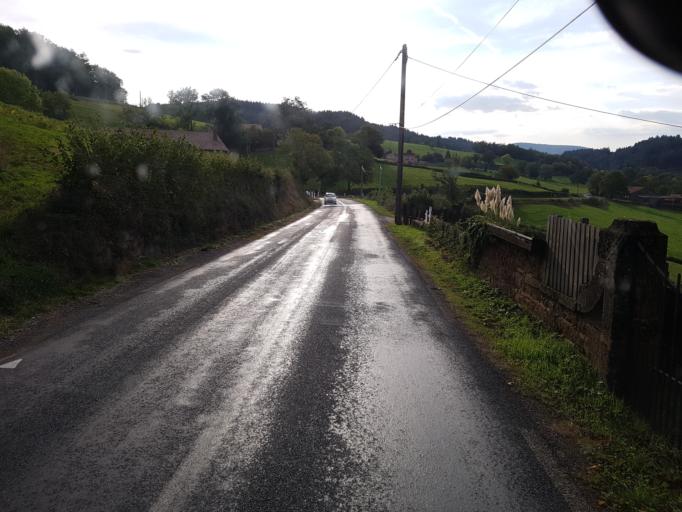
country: FR
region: Bourgogne
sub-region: Departement de Saone-et-Loire
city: Chauffailles
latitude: 46.2481
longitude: 4.4046
